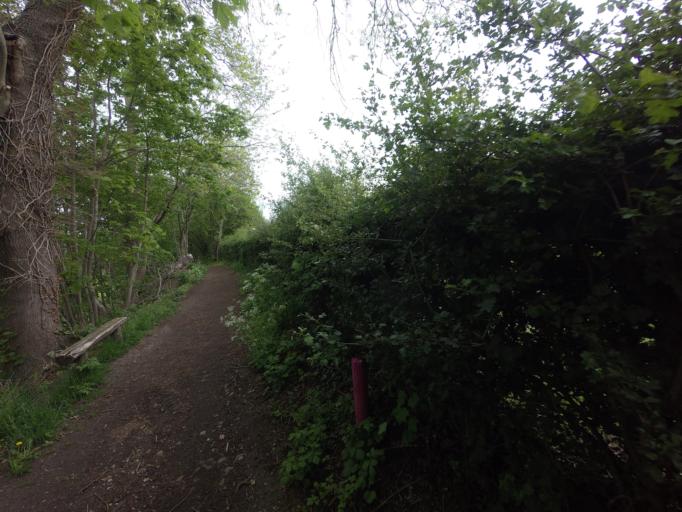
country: NL
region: Limburg
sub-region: Gemeente Maastricht
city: Heer
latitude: 50.8399
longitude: 5.7571
